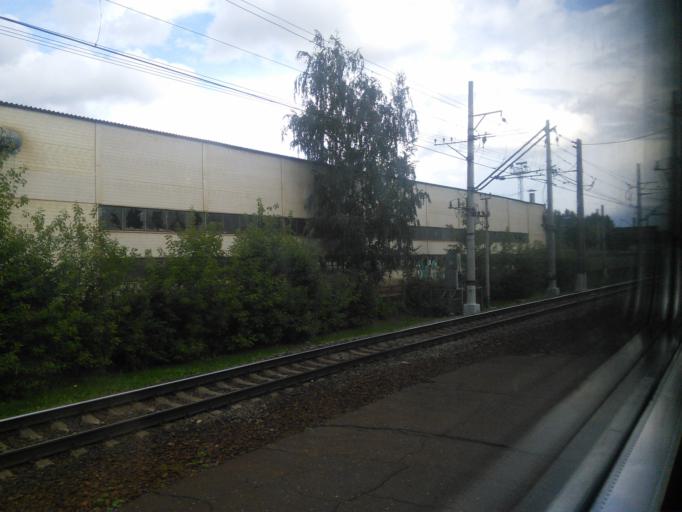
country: RU
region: Moscow
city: Ryazanskiy
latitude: 55.7439
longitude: 37.7422
